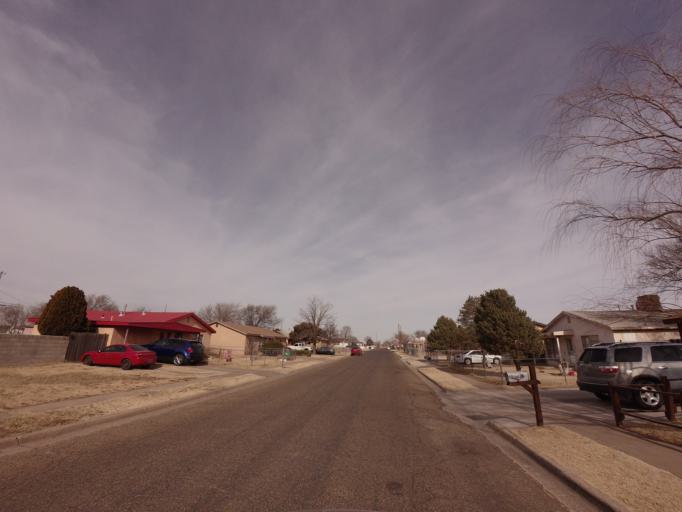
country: US
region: New Mexico
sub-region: Curry County
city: Clovis
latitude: 34.4091
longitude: -103.2374
